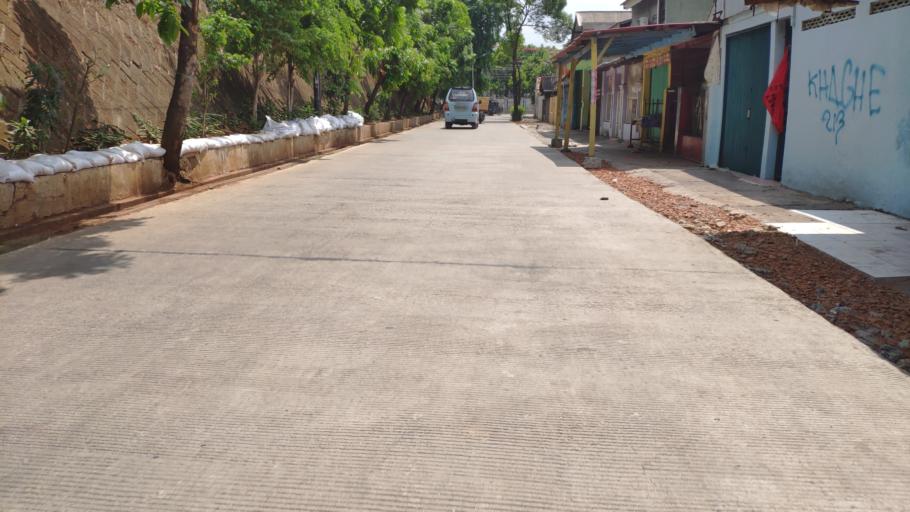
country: ID
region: Jakarta Raya
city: Jakarta
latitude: -6.2139
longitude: 106.8737
